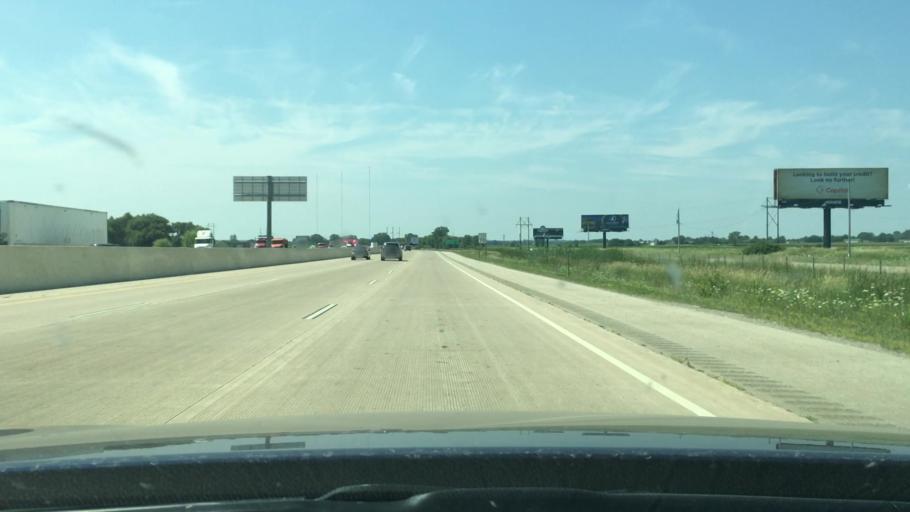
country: US
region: Wisconsin
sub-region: Winnebago County
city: Oshkosh
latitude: 44.0898
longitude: -88.5539
